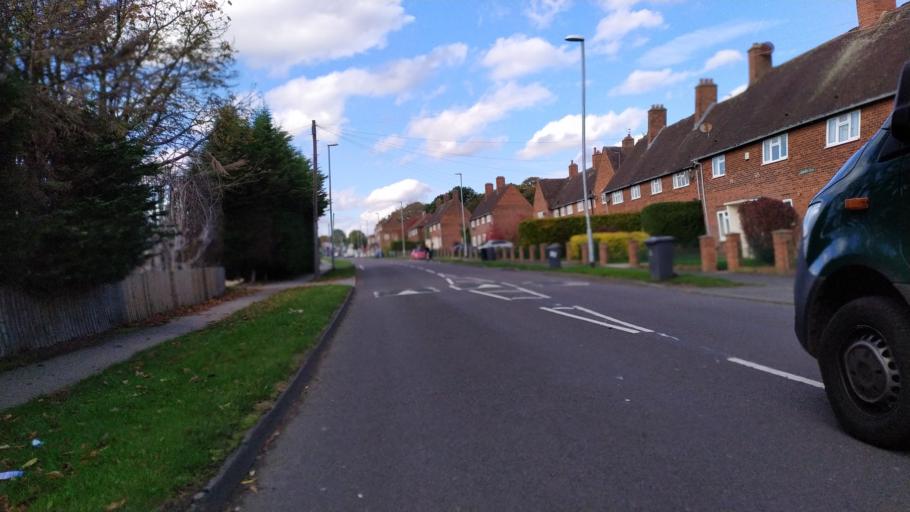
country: GB
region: England
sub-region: City and Borough of Leeds
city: Horsforth
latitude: 53.8202
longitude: -1.5944
